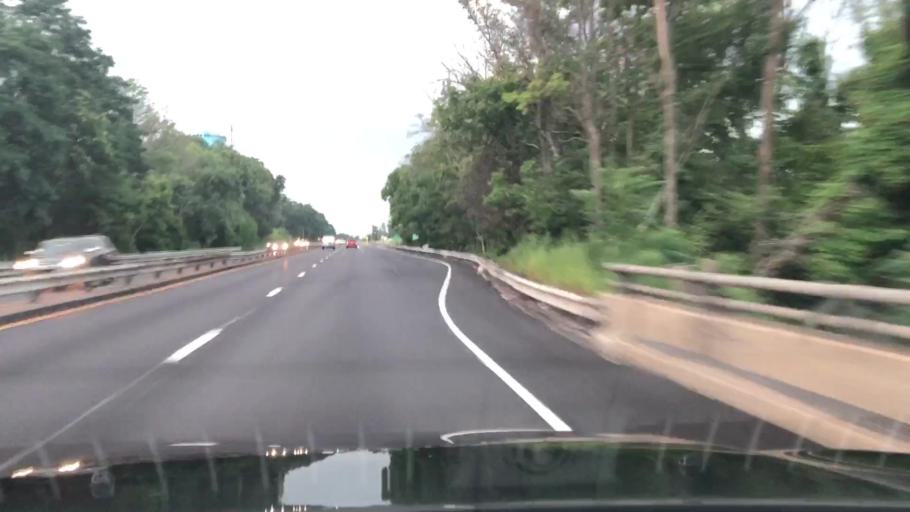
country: US
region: Pennsylvania
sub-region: Bucks County
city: Trevose
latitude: 40.1481
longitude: -74.9514
